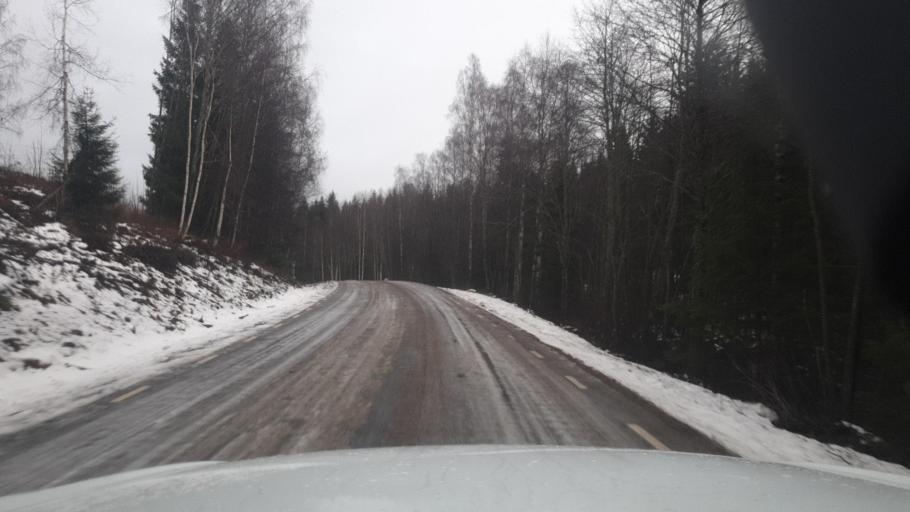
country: SE
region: Vaermland
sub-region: Torsby Kommun
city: Torsby
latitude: 59.9785
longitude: 12.8113
